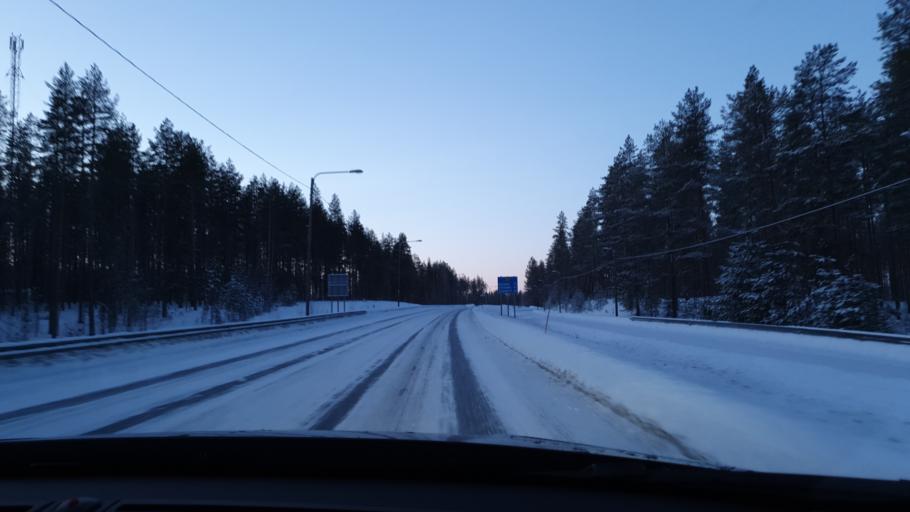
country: FI
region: Kainuu
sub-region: Kehys-Kainuu
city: Kuhmo
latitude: 64.0971
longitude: 29.4701
